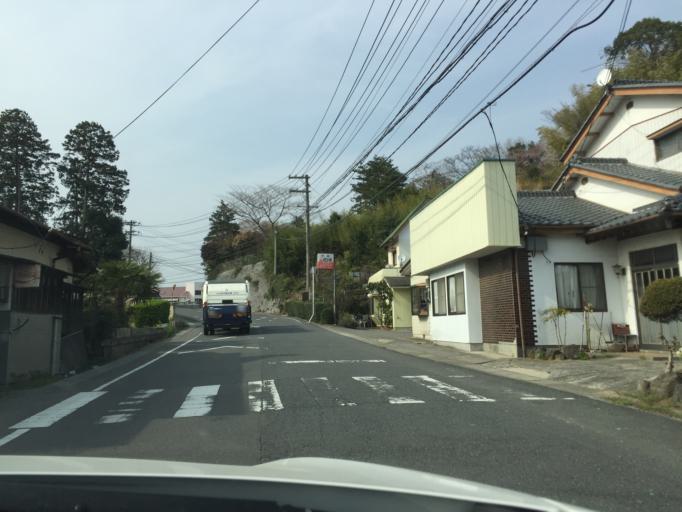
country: JP
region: Fukushima
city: Iwaki
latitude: 36.9804
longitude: 140.8548
